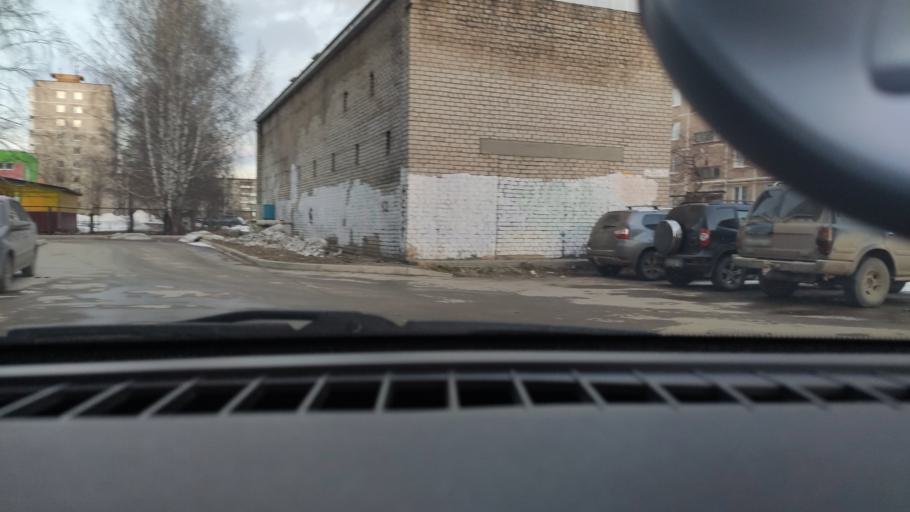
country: RU
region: Perm
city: Perm
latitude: 58.0867
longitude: 56.4081
